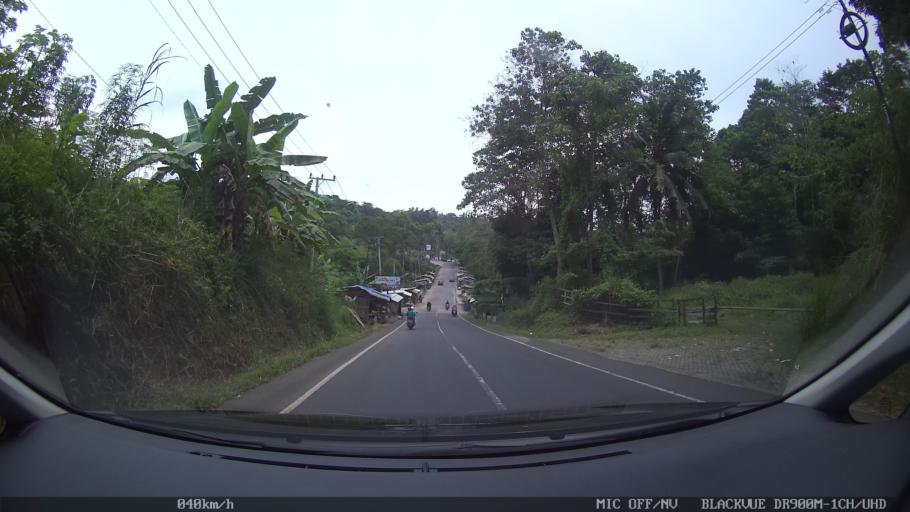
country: ID
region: Lampung
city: Bandarlampung
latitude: -5.4139
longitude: 105.2280
